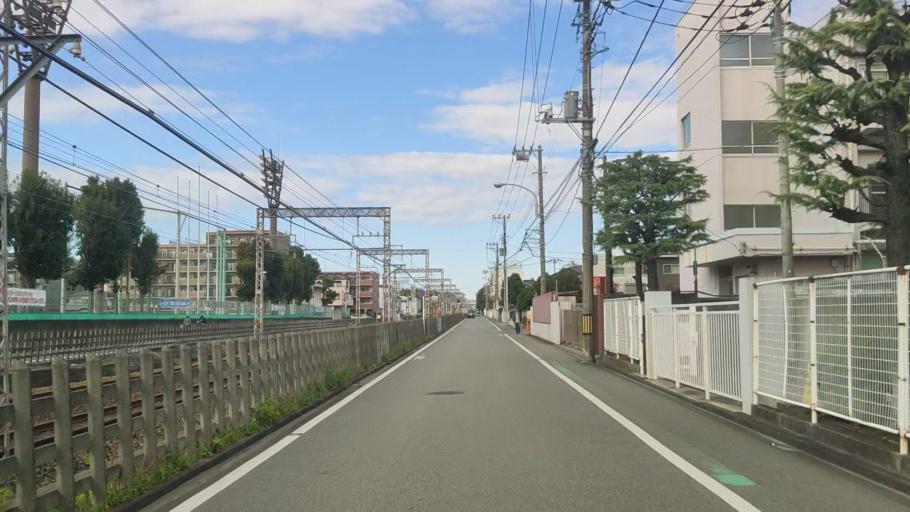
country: JP
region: Kanagawa
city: Minami-rinkan
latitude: 35.4750
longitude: 139.4589
